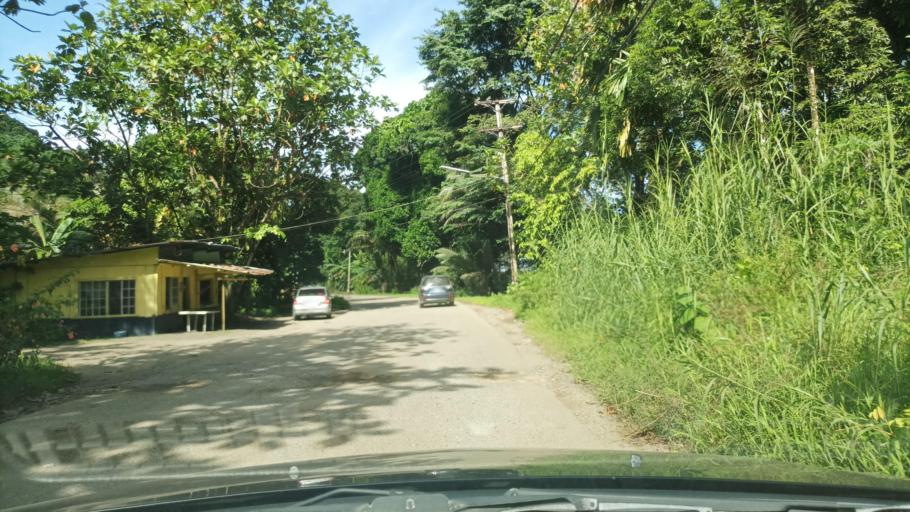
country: FM
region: Kosrae
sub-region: Lelu Municipality
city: Tofol
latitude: 5.3341
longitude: 163.0074
